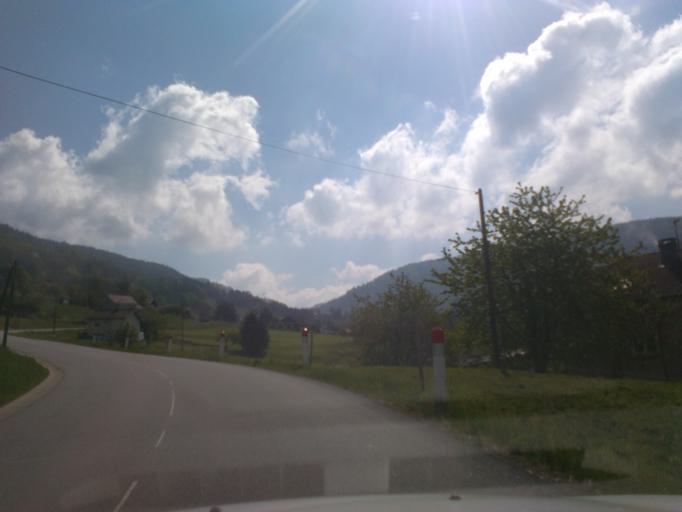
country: FR
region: Lorraine
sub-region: Departement des Vosges
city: Vagney
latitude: 47.9906
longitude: 6.7461
